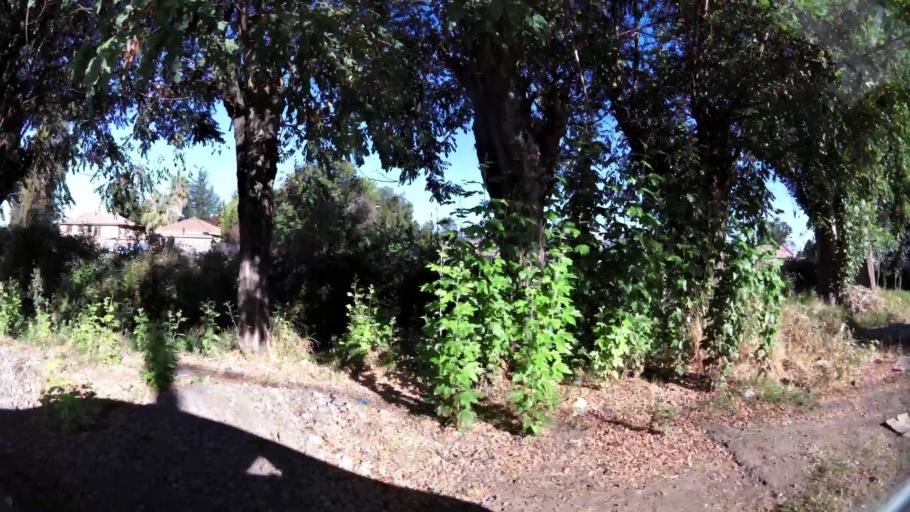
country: CL
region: O'Higgins
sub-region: Provincia de Cachapoal
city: Rancagua
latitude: -34.1751
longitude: -70.7249
